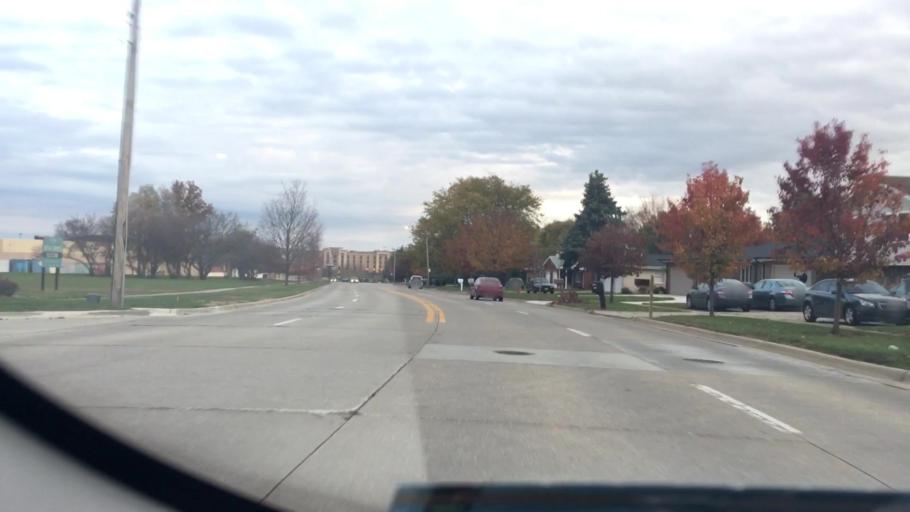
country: US
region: Illinois
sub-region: McLean County
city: Normal
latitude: 40.5079
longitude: -88.9603
